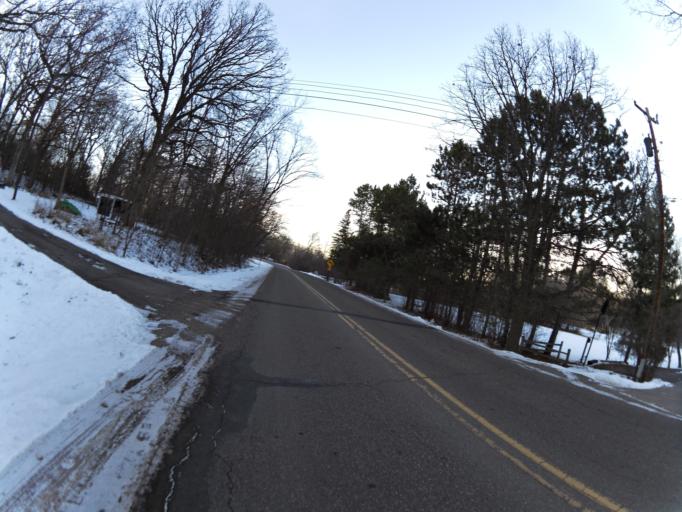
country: US
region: Minnesota
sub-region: Washington County
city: Lake Elmo
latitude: 44.9766
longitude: -92.8379
